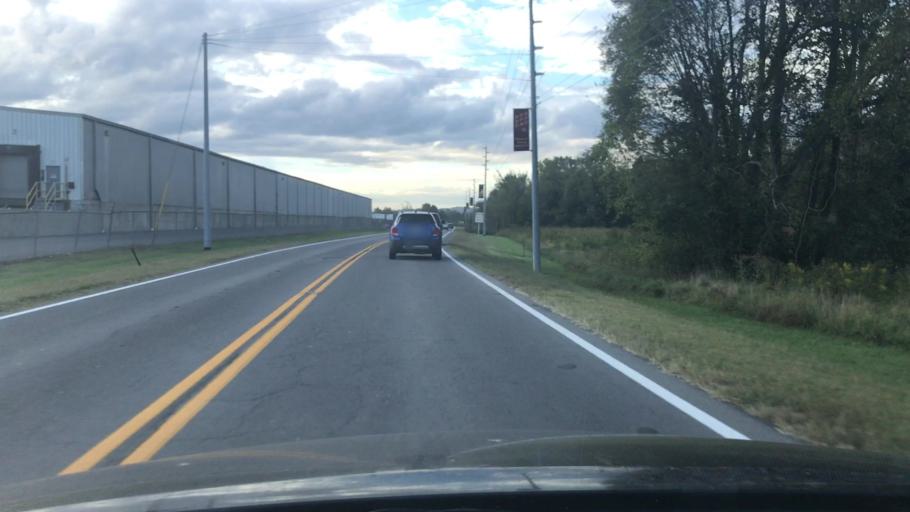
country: US
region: Tennessee
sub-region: Cheatham County
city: Ashland City
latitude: 36.2664
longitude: -87.0672
